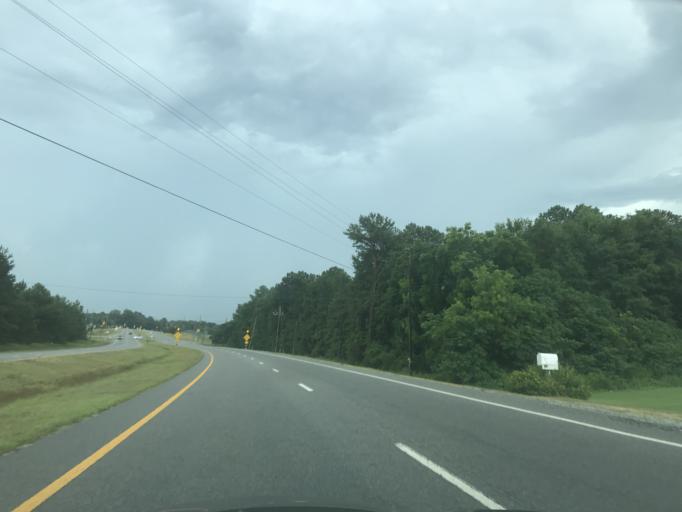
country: US
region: North Carolina
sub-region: Johnston County
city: Wilsons Mills
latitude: 35.5571
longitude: -78.3888
